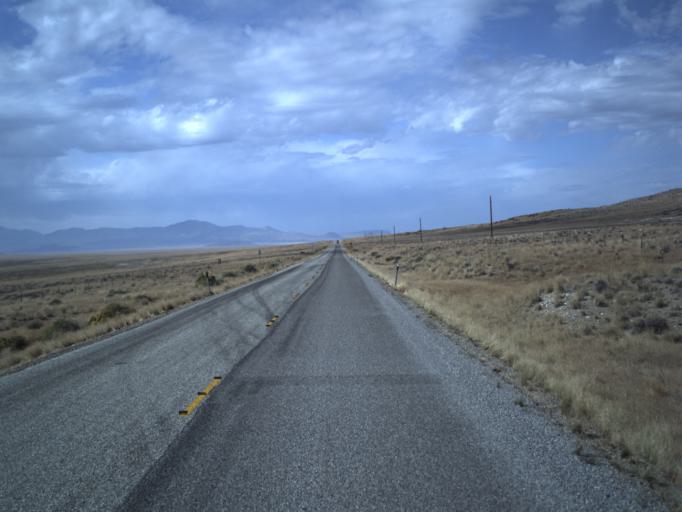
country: US
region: Utah
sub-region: Tooele County
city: Wendover
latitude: 41.4491
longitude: -113.6751
